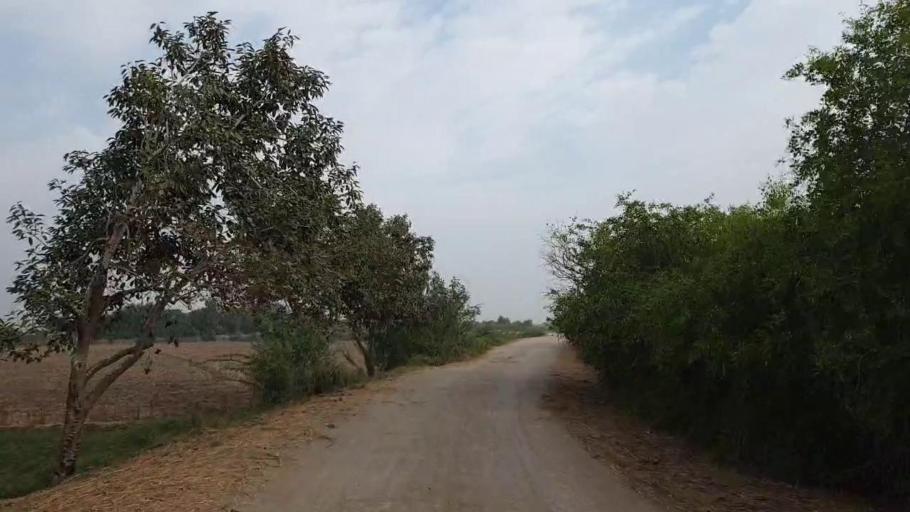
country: PK
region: Sindh
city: Tando Muhammad Khan
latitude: 25.0932
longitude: 68.4177
